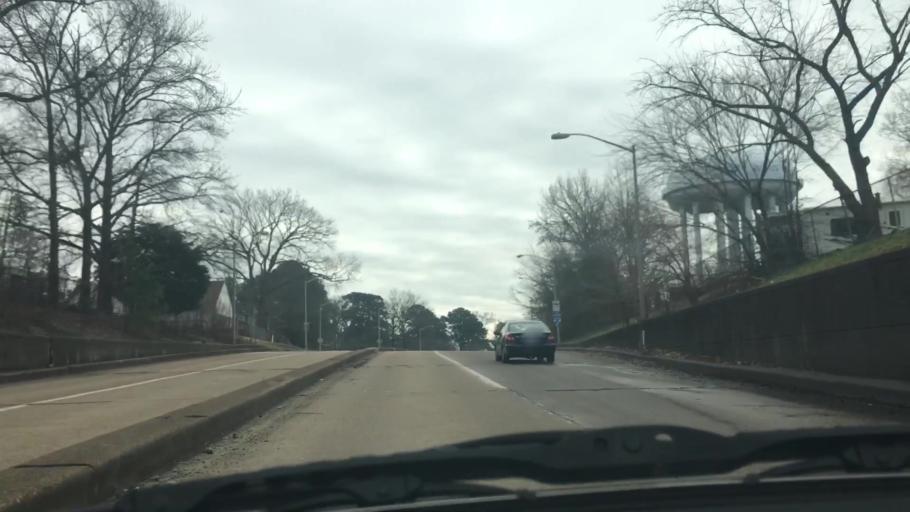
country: US
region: Virginia
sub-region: City of Norfolk
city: Norfolk
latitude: 36.9495
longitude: -76.2589
